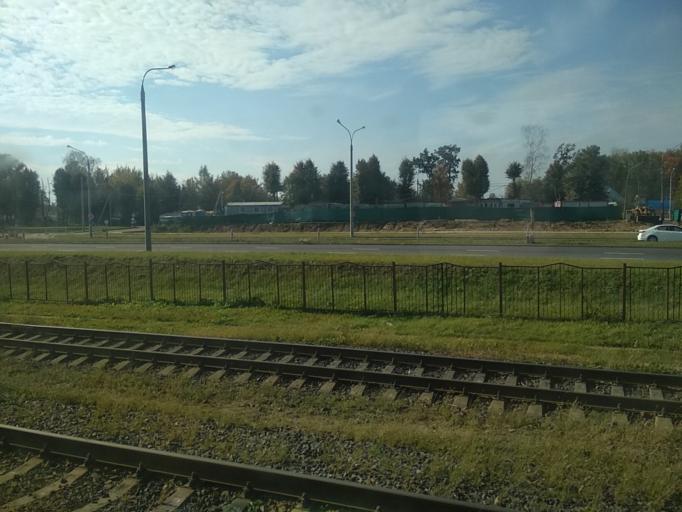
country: BY
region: Minsk
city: Minsk
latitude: 53.8675
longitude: 27.5609
